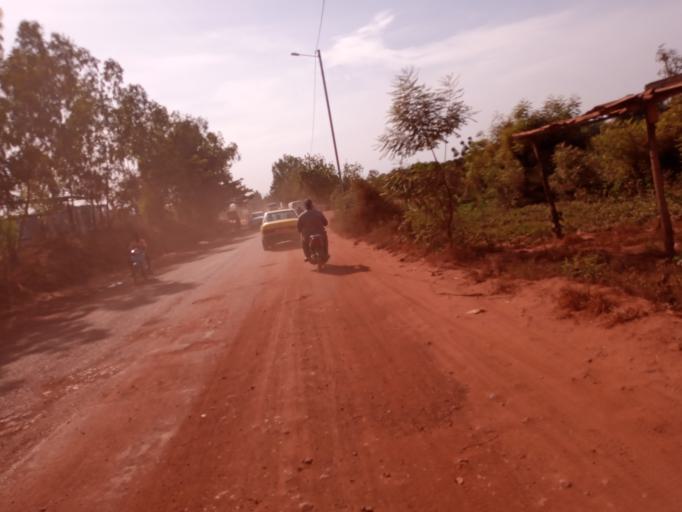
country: ML
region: Bamako
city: Bamako
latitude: 12.6346
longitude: -7.9349
